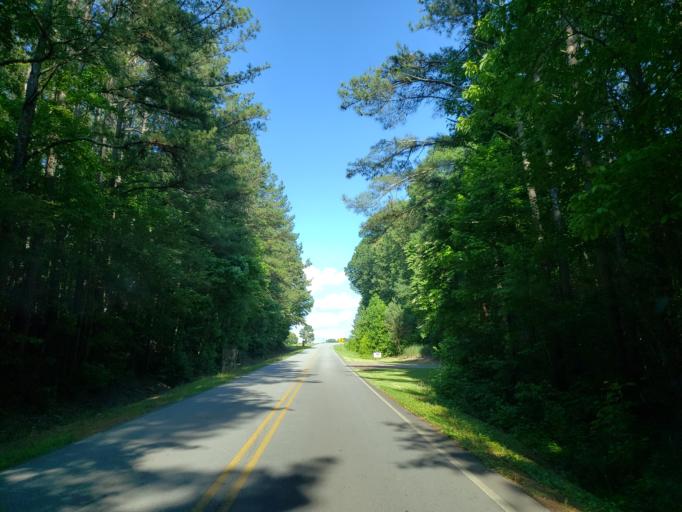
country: US
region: Georgia
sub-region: Haralson County
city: Bremen
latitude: 33.6844
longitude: -85.0922
